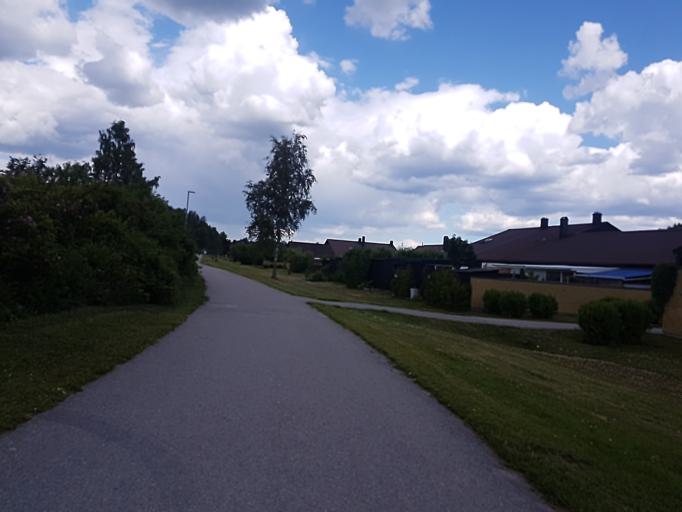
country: SE
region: Soedermanland
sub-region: Gnesta Kommun
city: Gnesta
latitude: 59.0365
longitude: 17.3278
